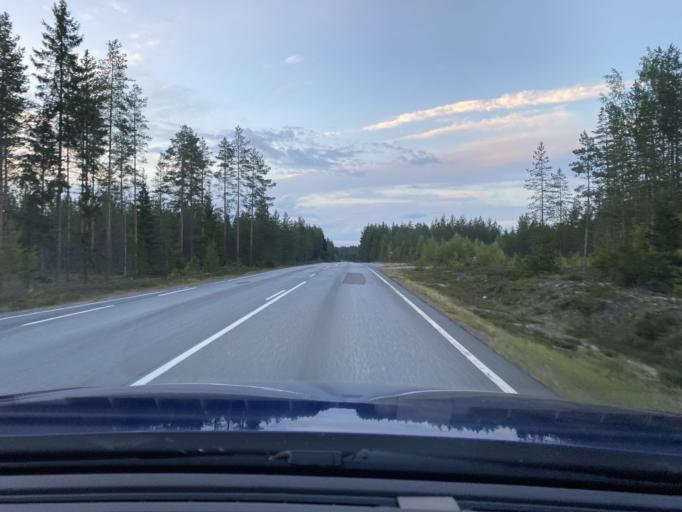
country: FI
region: Satakunta
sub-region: Pohjois-Satakunta
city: Honkajoki
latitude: 62.0317
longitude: 22.2362
